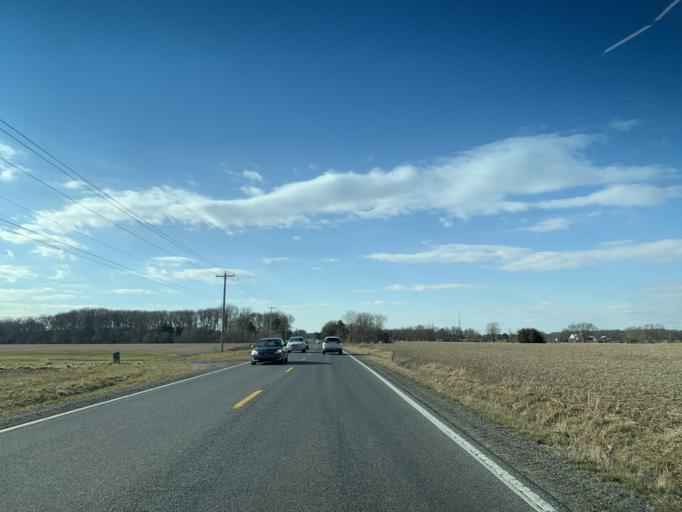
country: US
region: Maryland
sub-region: Queen Anne's County
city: Centreville
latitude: 39.0178
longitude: -76.0046
